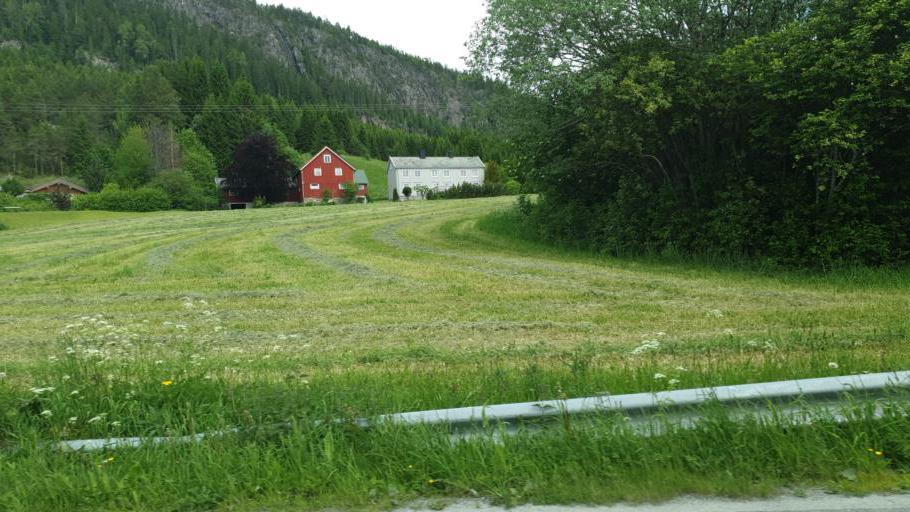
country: NO
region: Sor-Trondelag
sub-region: Trondheim
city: Trondheim
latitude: 63.5759
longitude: 10.3725
